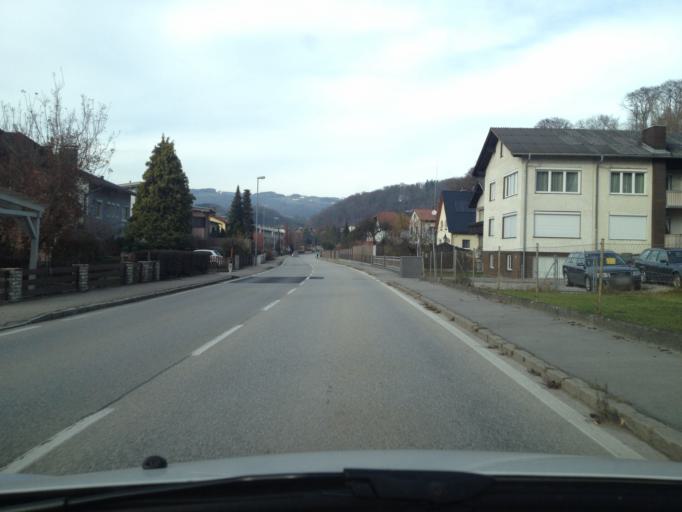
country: AT
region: Upper Austria
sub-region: Politischer Bezirk Urfahr-Umgebung
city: Steyregg
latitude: 48.3230
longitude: 14.3405
